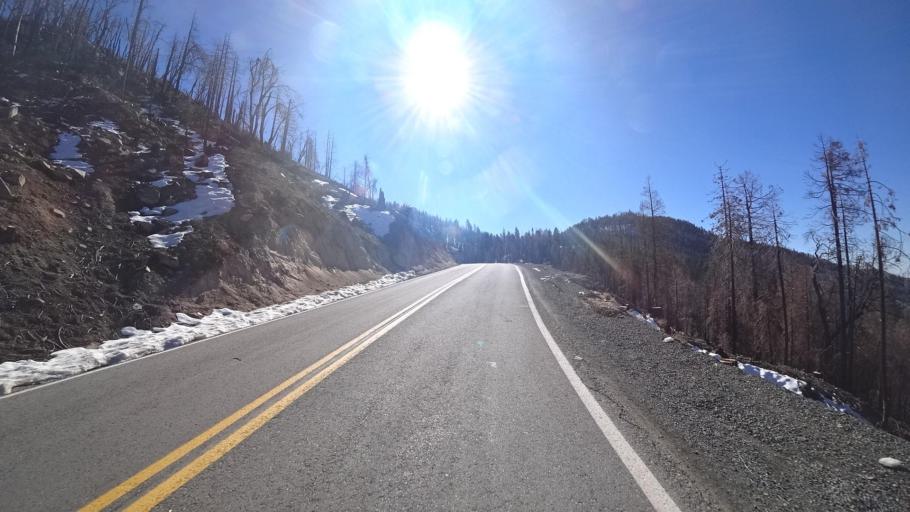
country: US
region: California
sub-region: Kern County
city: Alta Sierra
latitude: 35.7488
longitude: -118.5581
